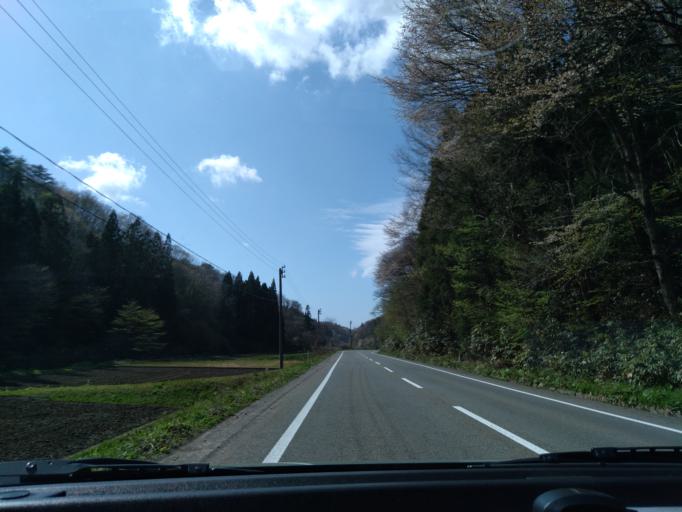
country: JP
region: Akita
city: Akita
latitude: 39.7029
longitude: 140.2158
